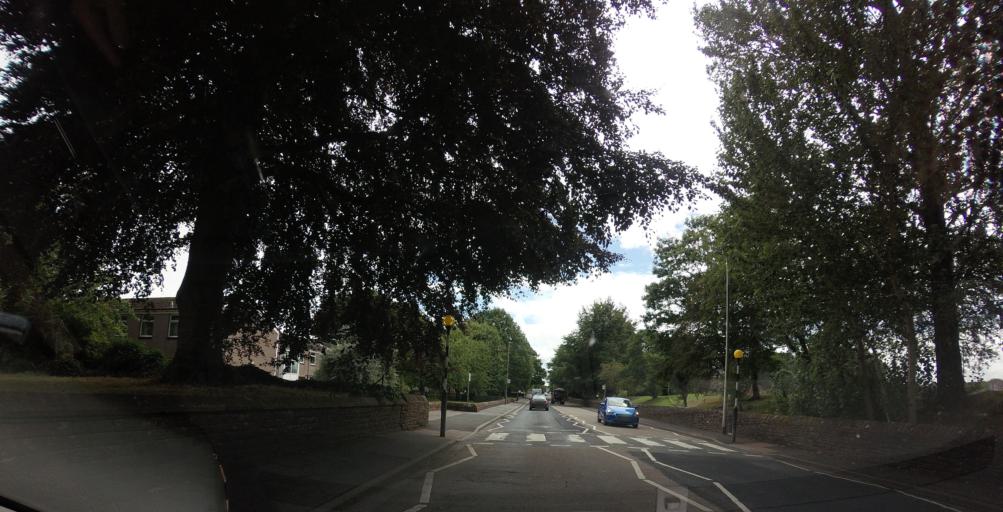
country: GB
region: England
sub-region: Cumbria
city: Penrith
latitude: 54.6593
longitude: -2.7470
